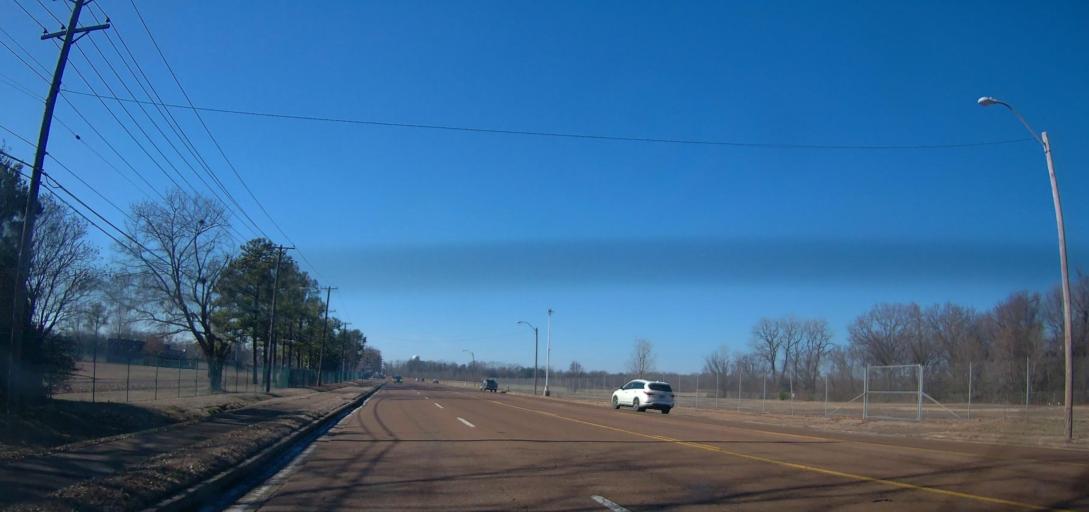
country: US
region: Tennessee
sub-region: Shelby County
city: Millington
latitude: 35.3405
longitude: -89.8787
